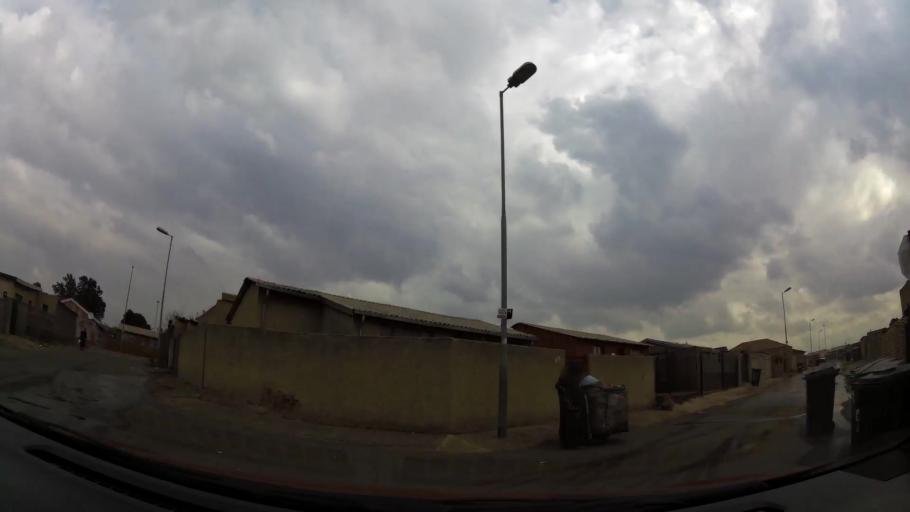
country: ZA
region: Gauteng
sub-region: City of Johannesburg Metropolitan Municipality
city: Soweto
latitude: -26.2614
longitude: 27.8374
